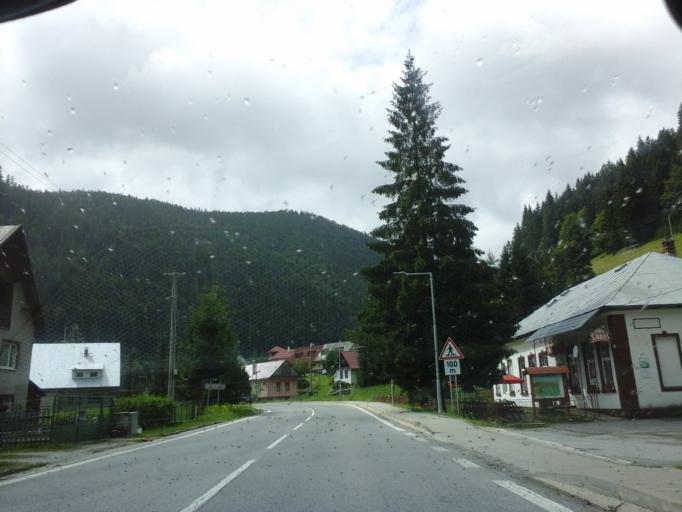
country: SK
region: Kosicky
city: Dobsina
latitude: 48.8713
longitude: 20.3390
